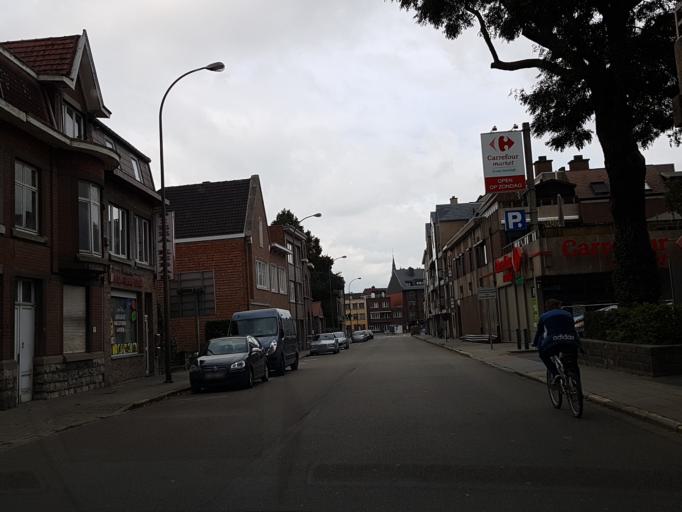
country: BE
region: Flanders
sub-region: Provincie Limburg
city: Sint-Truiden
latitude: 50.8113
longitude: 5.1902
